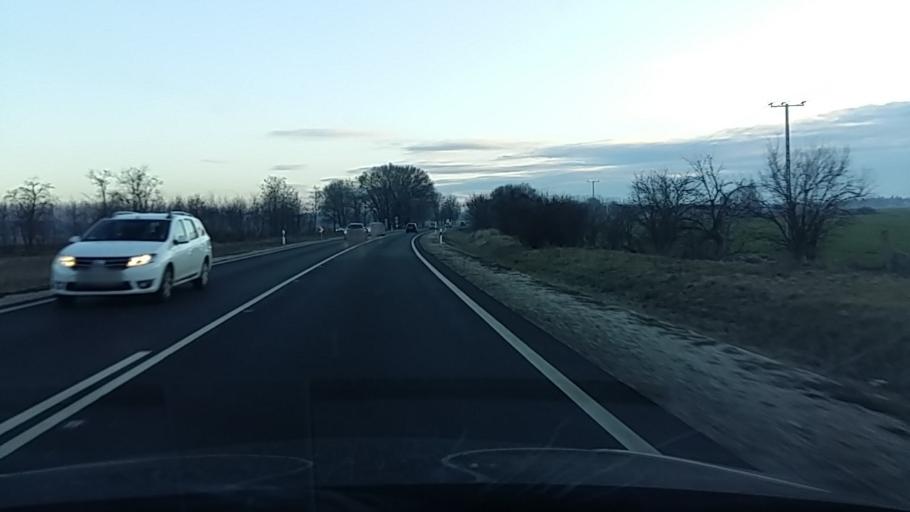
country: HU
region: Hajdu-Bihar
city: Hajduhadhaz
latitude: 47.6593
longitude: 21.6605
